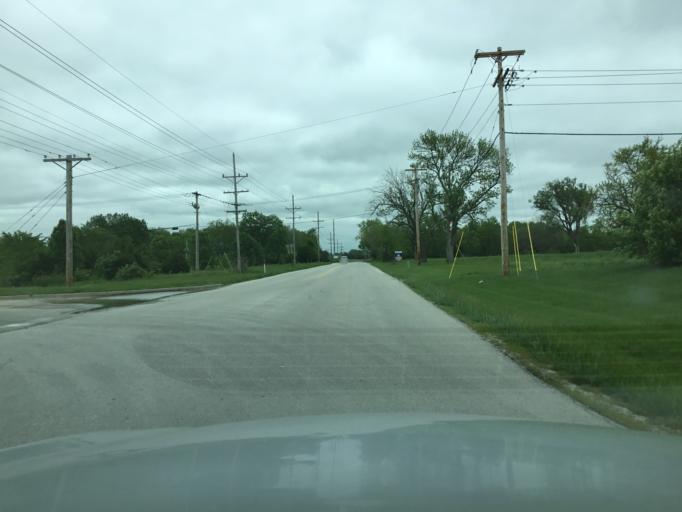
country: US
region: Kansas
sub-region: Franklin County
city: Ottawa
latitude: 38.5793
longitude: -95.2640
